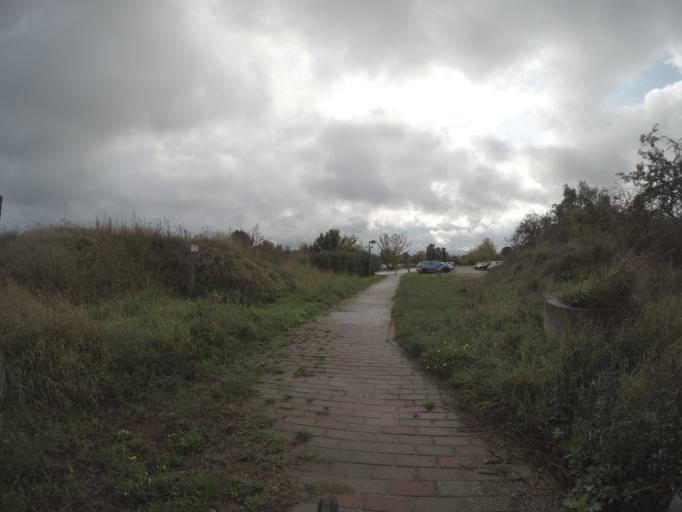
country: DE
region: Berlin
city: Blankenfelde
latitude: 52.6617
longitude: 13.3872
